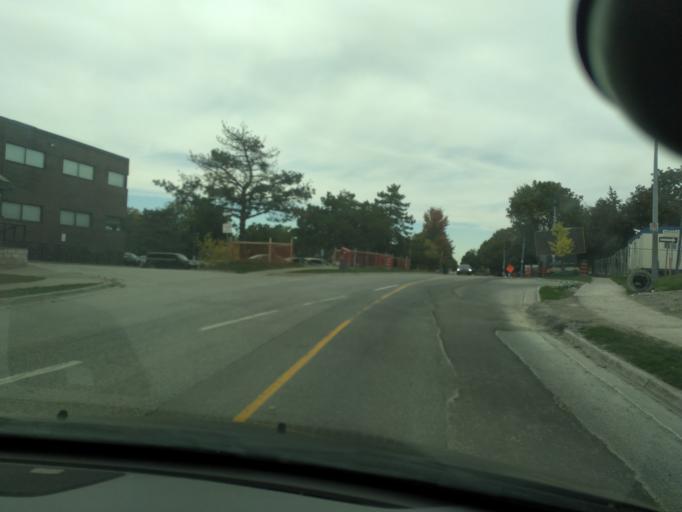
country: CA
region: Ontario
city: Newmarket
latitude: 44.0623
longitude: -79.4495
